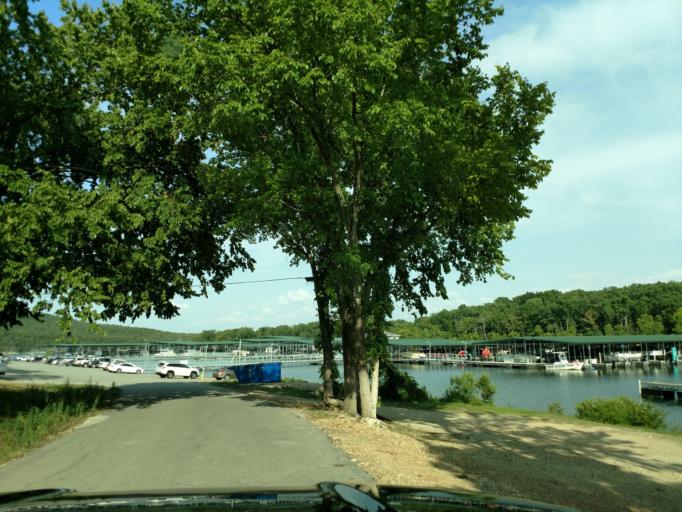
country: US
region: Missouri
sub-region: Barry County
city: Shell Knob
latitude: 36.5951
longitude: -93.5509
